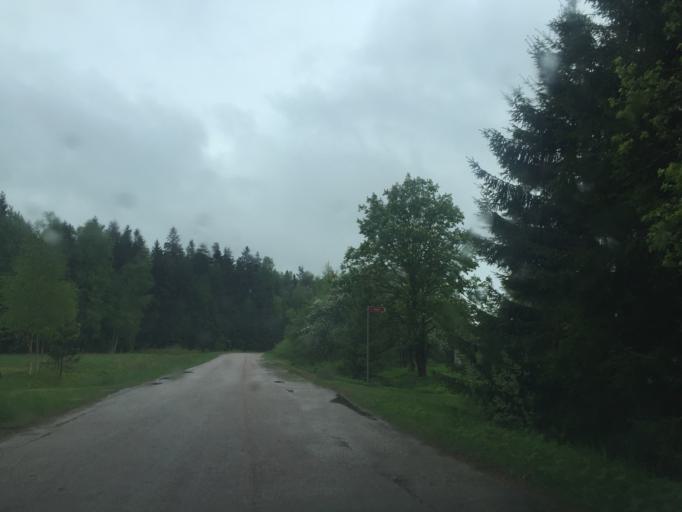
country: LV
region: Ogre
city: Jumprava
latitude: 56.6775
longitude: 24.9827
